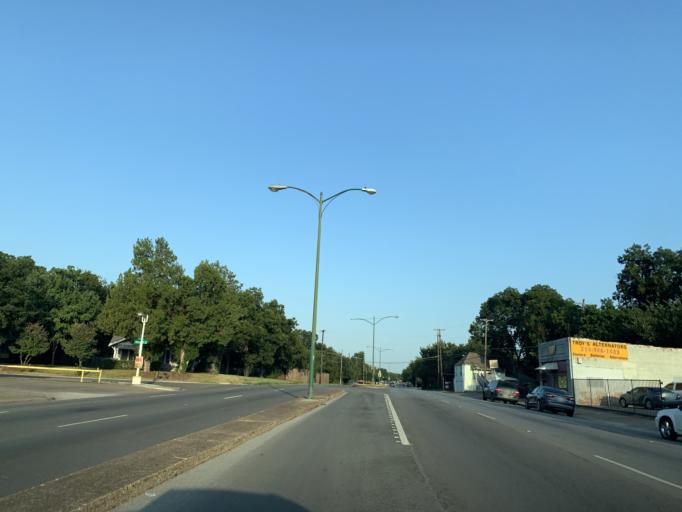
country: US
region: Texas
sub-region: Dallas County
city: Cockrell Hill
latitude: 32.7464
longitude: -96.8508
